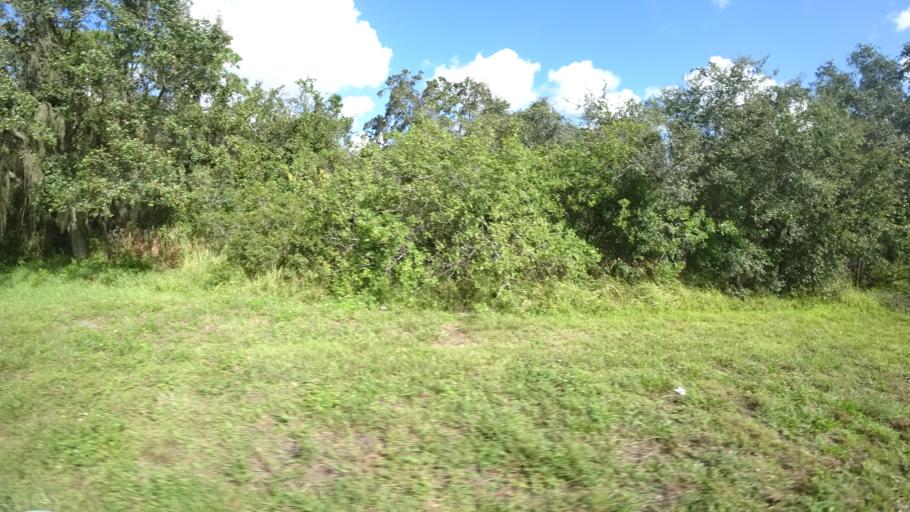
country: US
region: Florida
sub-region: Sarasota County
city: Lake Sarasota
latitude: 27.3465
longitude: -82.2421
